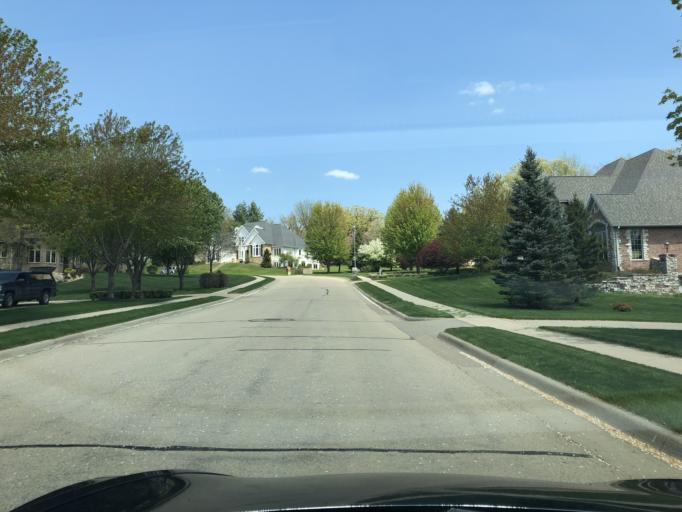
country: US
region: Illinois
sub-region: Jo Daviess County
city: East Dubuque
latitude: 42.4741
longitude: -90.6623
